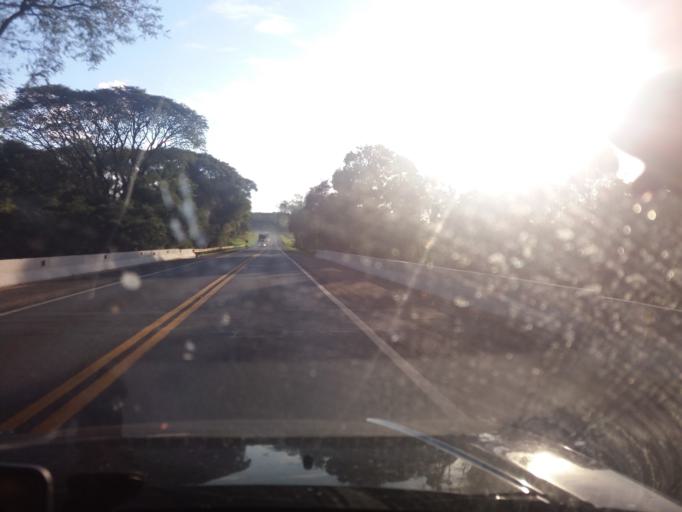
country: BR
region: Sao Paulo
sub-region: Buri
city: Buri
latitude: -23.9280
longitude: -48.6566
